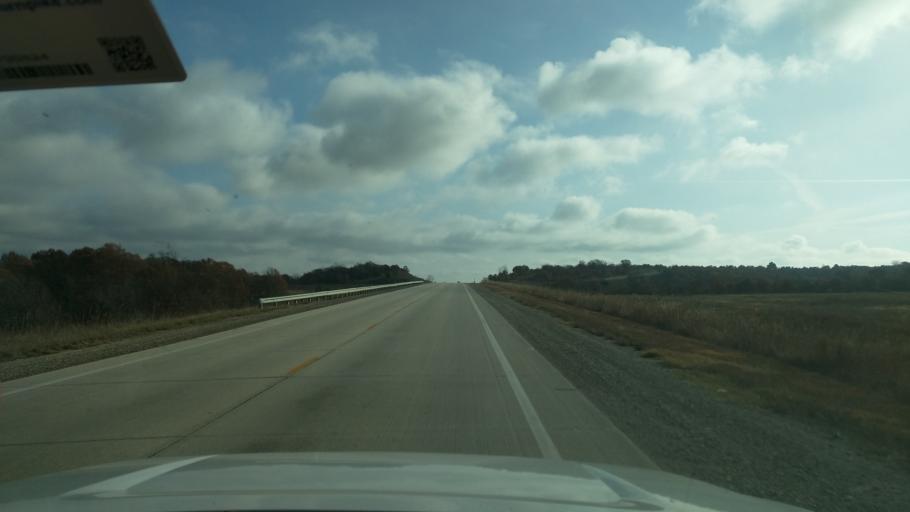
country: US
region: Kansas
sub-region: Chautauqua County
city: Sedan
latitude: 37.0825
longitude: -96.1213
